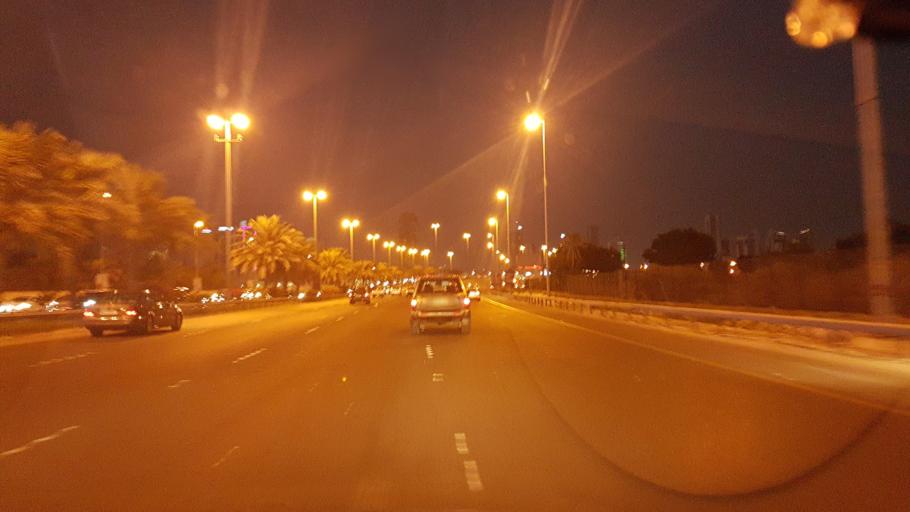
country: BH
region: Manama
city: Jidd Hafs
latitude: 26.2278
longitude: 50.5286
